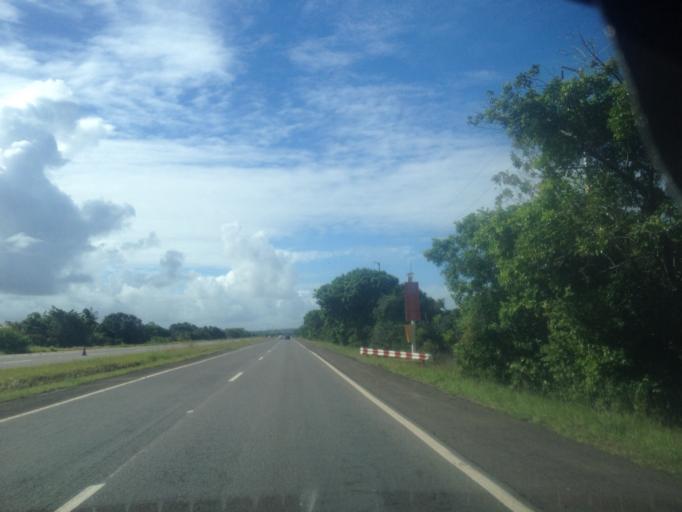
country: BR
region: Bahia
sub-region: Mata De Sao Joao
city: Mata de Sao Joao
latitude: -12.6274
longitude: -38.0629
